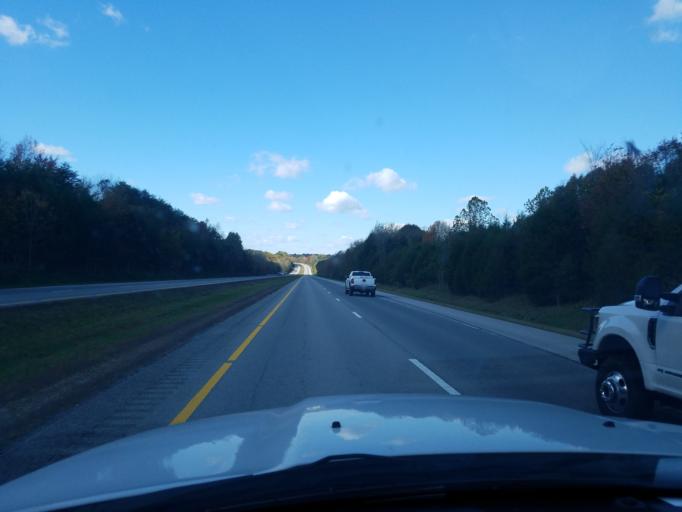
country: US
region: Kentucky
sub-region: Barren County
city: Glasgow
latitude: 36.9965
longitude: -85.7805
